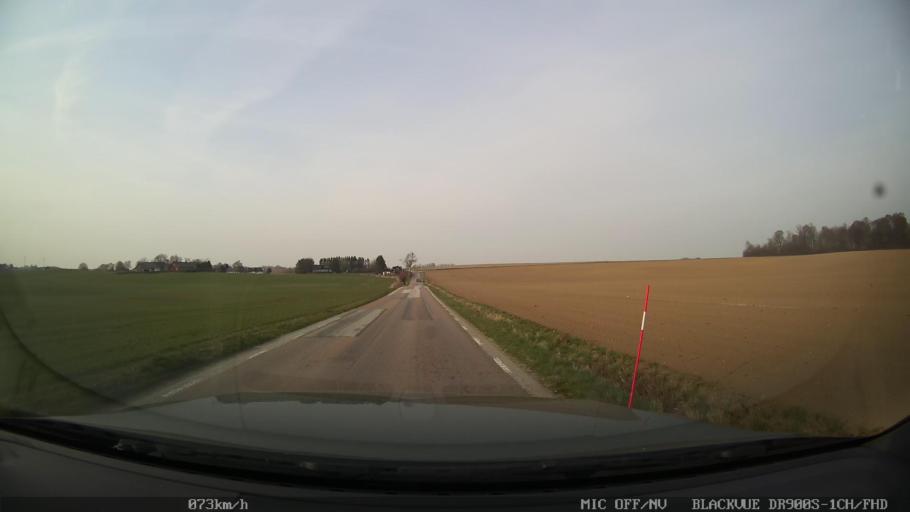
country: SE
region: Skane
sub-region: Ystads Kommun
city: Ystad
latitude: 55.4517
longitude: 13.8310
